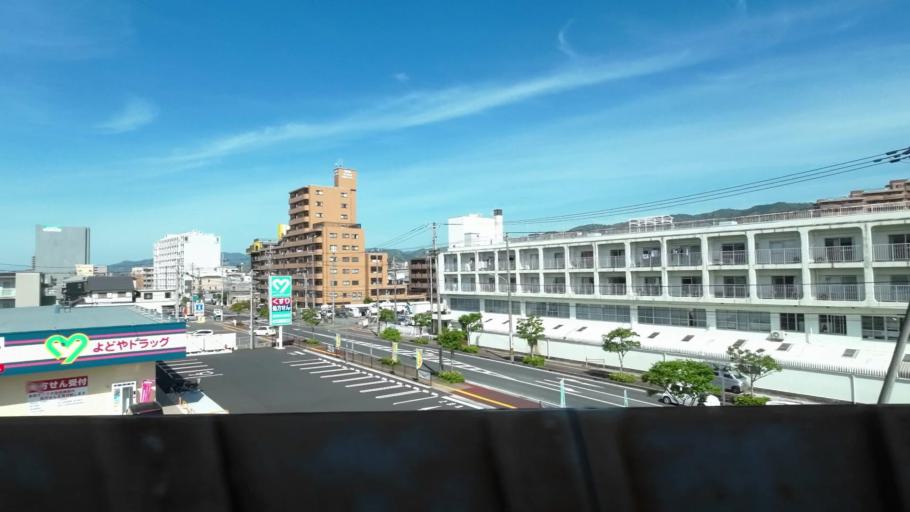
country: JP
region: Kochi
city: Kochi-shi
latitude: 33.5694
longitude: 133.5525
